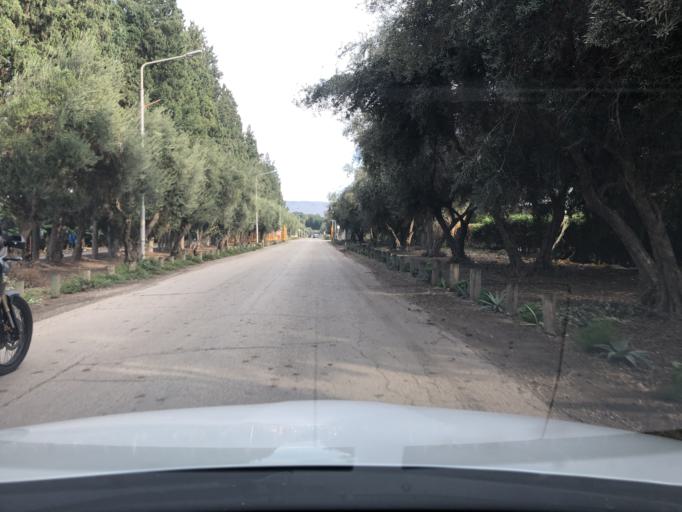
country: IL
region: Northern District
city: Yavne'el
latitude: 32.6589
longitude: 35.5752
